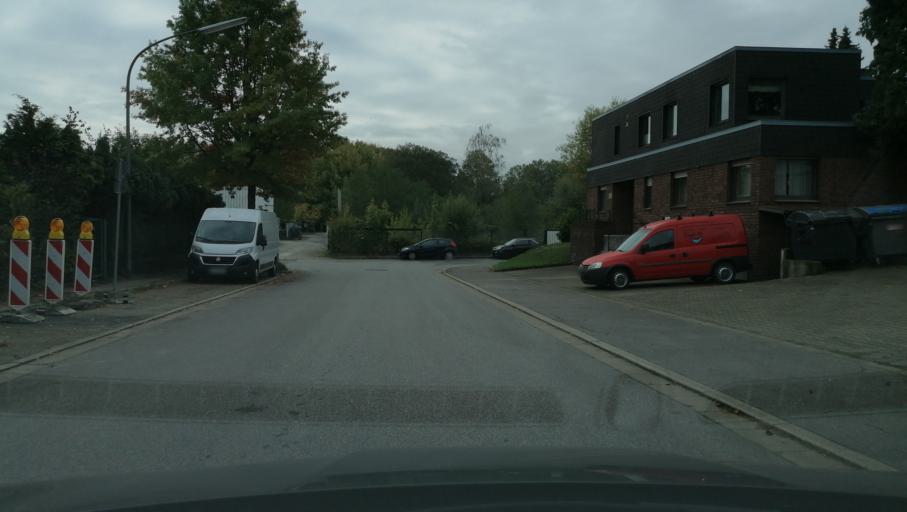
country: DE
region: North Rhine-Westphalia
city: Herten
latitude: 51.5841
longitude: 7.1123
